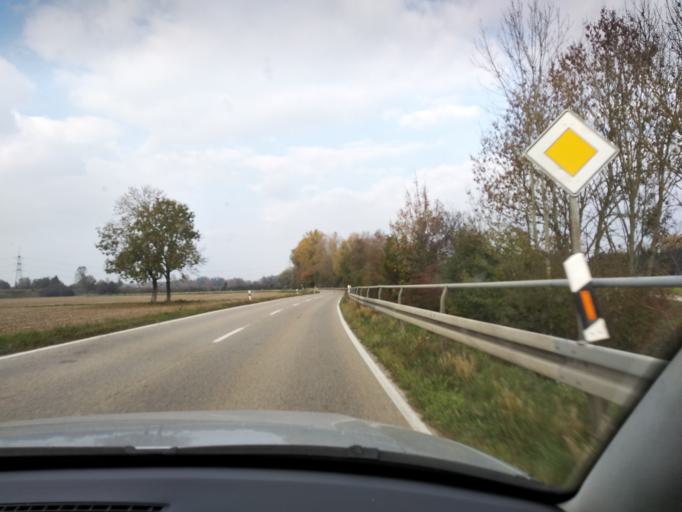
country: DE
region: Bavaria
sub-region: Upper Bavaria
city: Markt Schwaben
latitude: 48.1991
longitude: 11.8762
